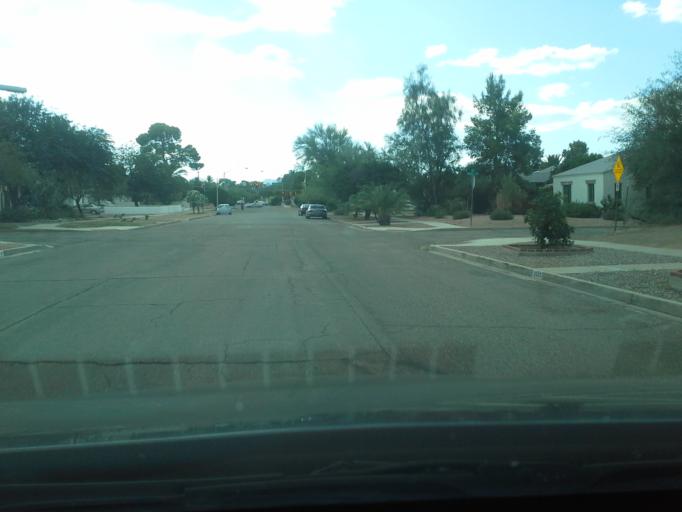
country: US
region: Arizona
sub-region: Pima County
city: Tucson
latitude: 32.2318
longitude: -110.9335
